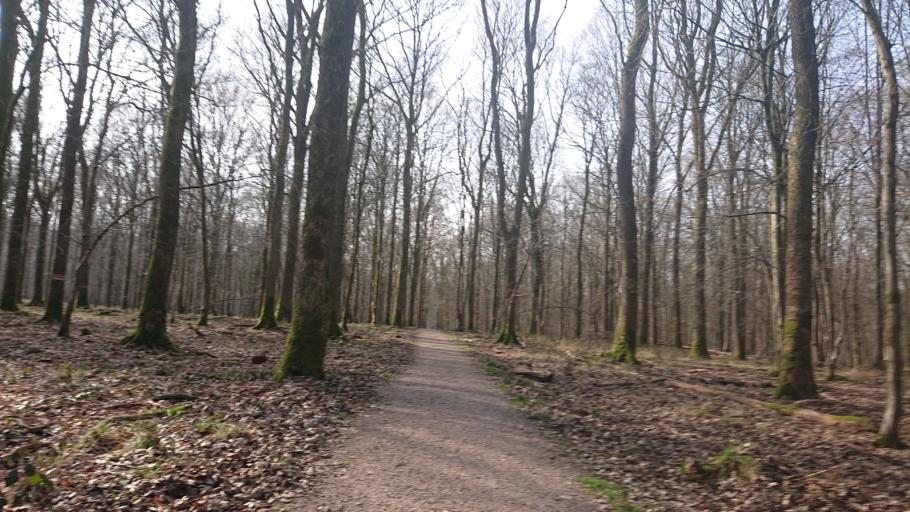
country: FR
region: Nord-Pas-de-Calais
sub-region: Departement du Nord
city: Maroilles
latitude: 50.1712
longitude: 3.7281
